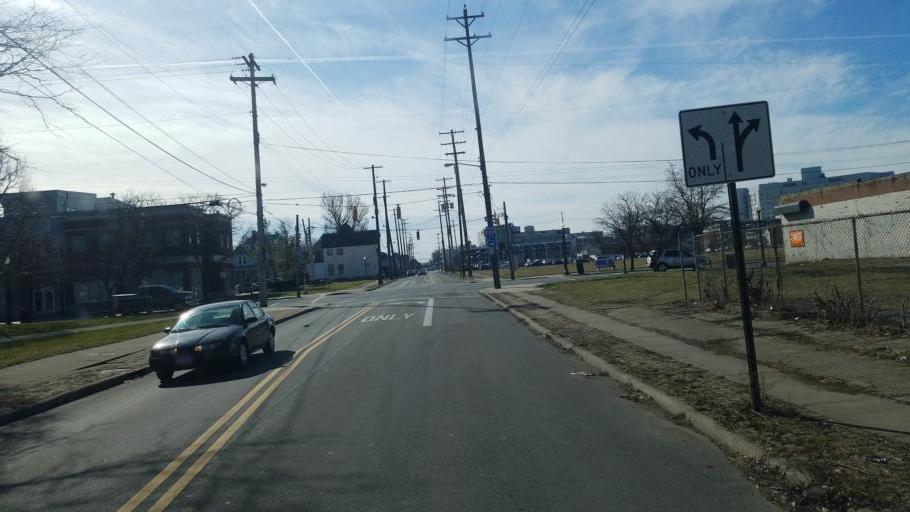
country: US
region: Ohio
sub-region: Franklin County
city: Columbus
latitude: 39.9585
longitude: -82.9761
